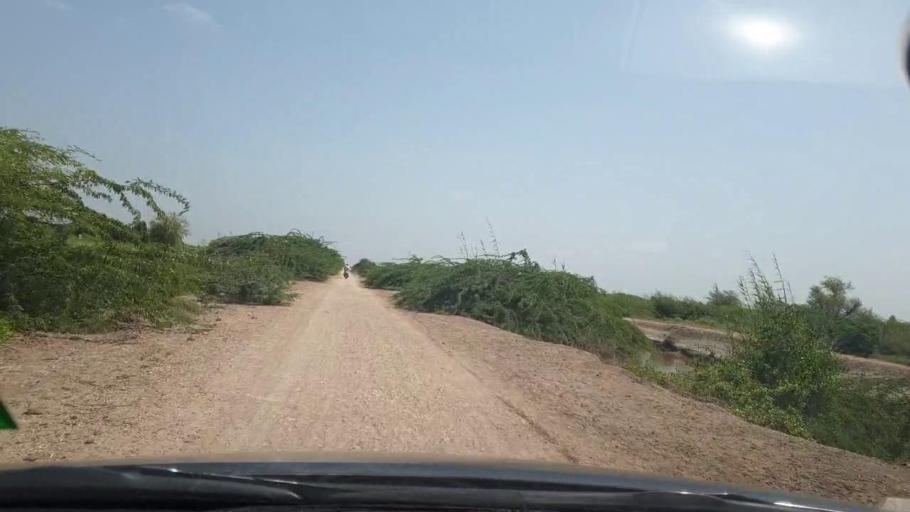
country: PK
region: Sindh
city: Tando Bago
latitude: 24.8950
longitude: 69.0891
